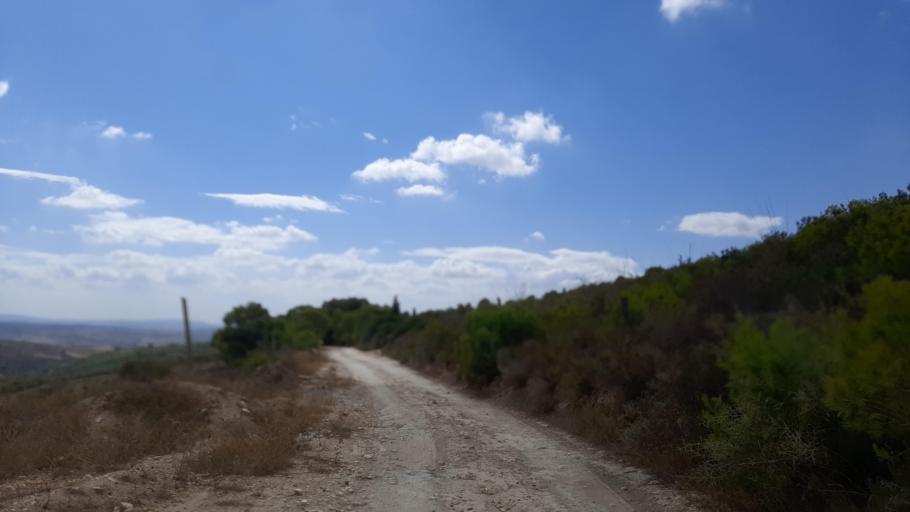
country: TN
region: Zaghwan
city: Zaghouan
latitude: 36.4944
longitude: 10.1744
